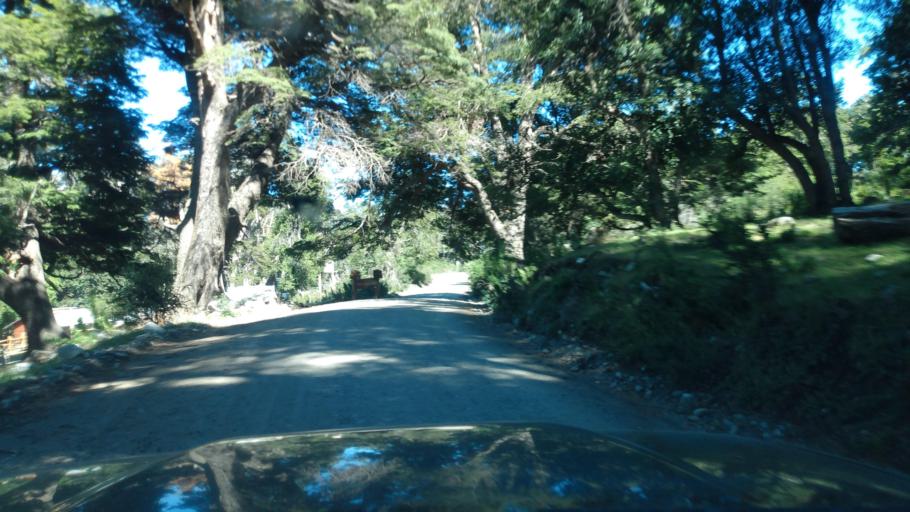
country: AR
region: Neuquen
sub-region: Departamento de Lacar
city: San Martin de los Andes
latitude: -39.7501
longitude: -71.4612
